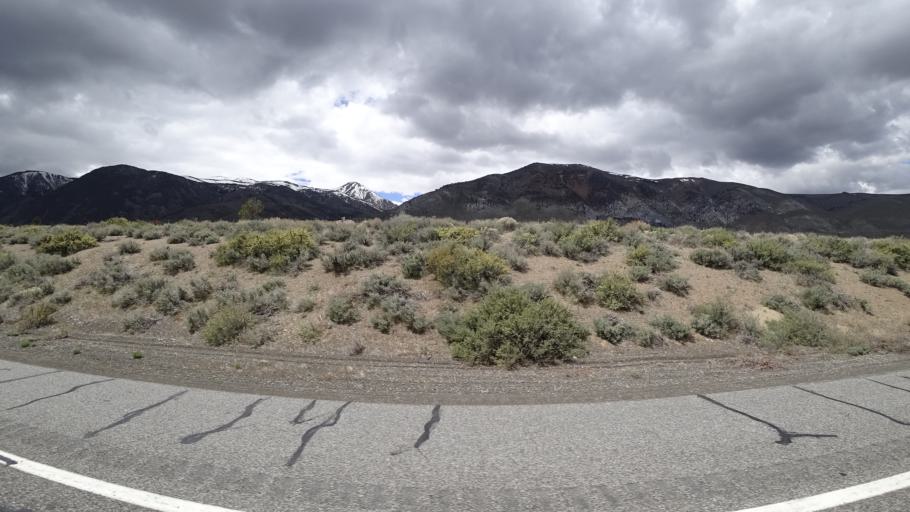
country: US
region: California
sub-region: Mono County
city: Bridgeport
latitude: 38.0420
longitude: -119.1593
